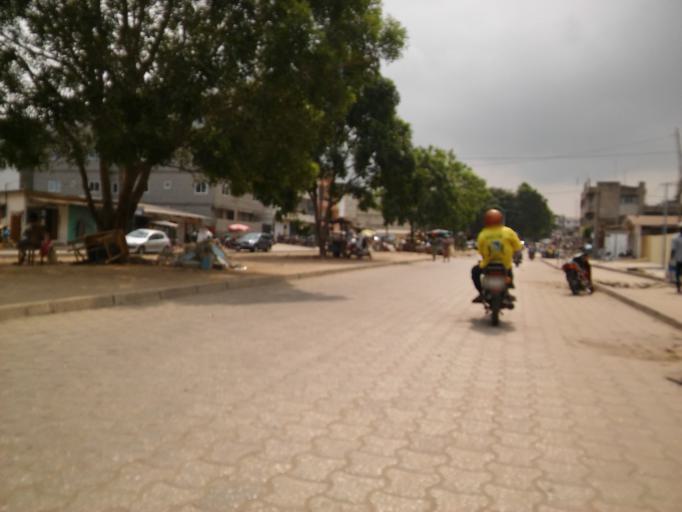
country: BJ
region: Littoral
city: Cotonou
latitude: 6.3854
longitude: 2.4153
